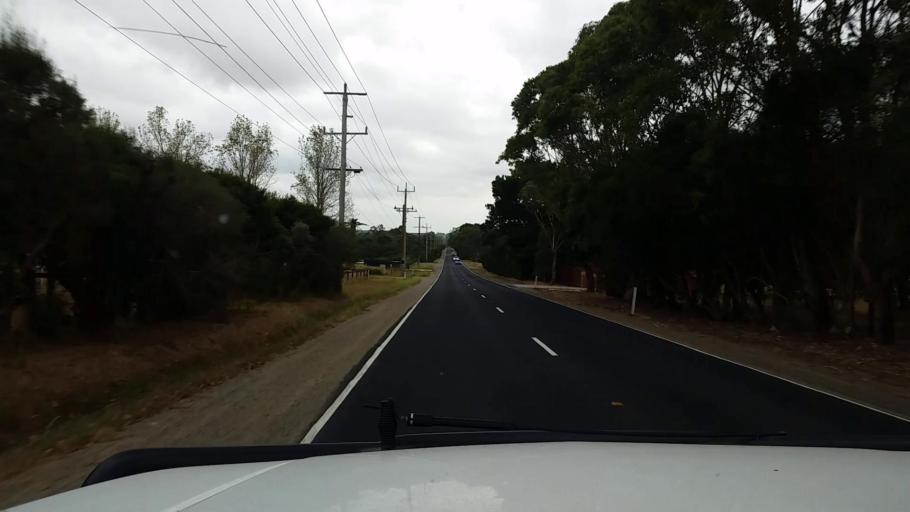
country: AU
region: Victoria
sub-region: Mornington Peninsula
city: Somerville
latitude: -38.2170
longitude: 145.1558
